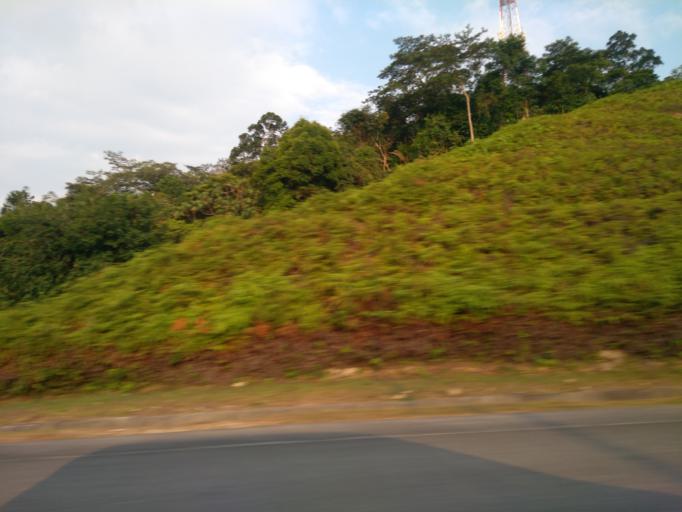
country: MY
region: Putrajaya
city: Putrajaya
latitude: 2.9815
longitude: 101.6827
